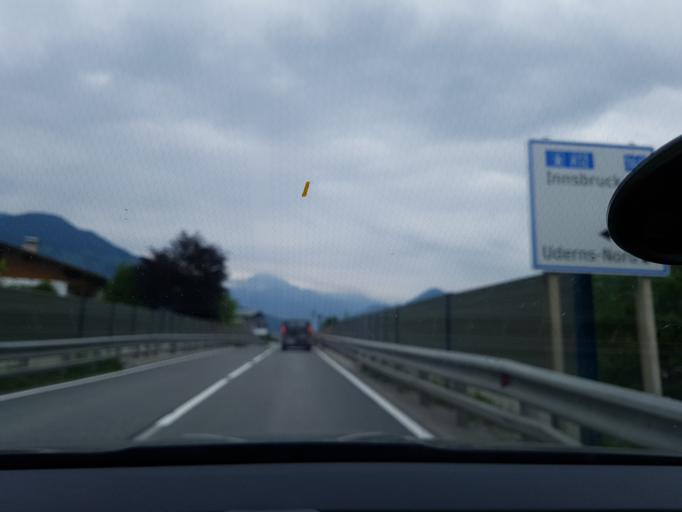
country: AT
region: Tyrol
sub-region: Politischer Bezirk Schwaz
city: Uderns
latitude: 47.3279
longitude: 11.8645
